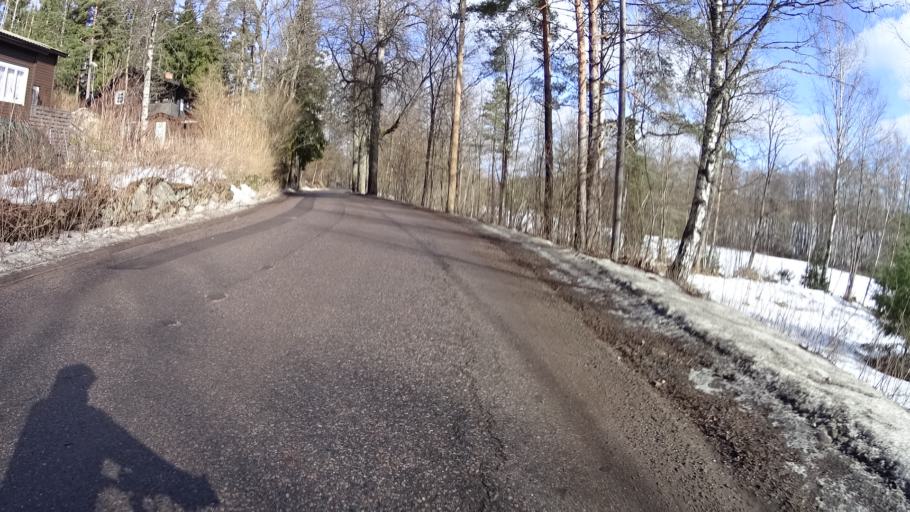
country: FI
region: Uusimaa
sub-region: Helsinki
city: Espoo
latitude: 60.2692
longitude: 24.6537
